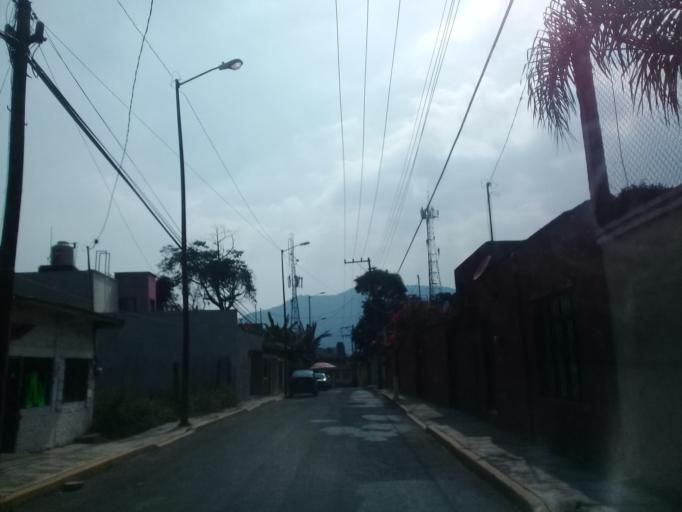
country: MX
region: Veracruz
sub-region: Mariano Escobedo
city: Palmira
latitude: 18.8740
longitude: -97.1033
